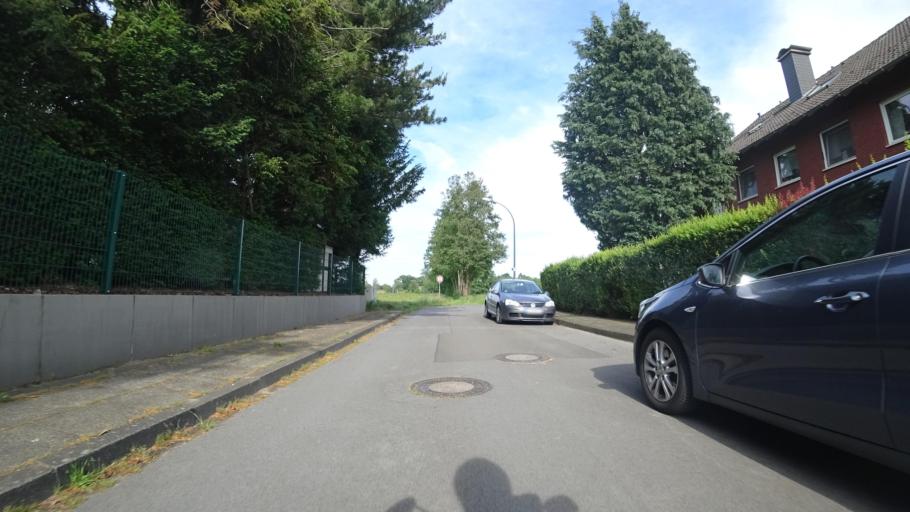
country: DE
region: North Rhine-Westphalia
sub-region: Regierungsbezirk Detmold
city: Guetersloh
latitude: 51.9038
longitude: 8.4422
